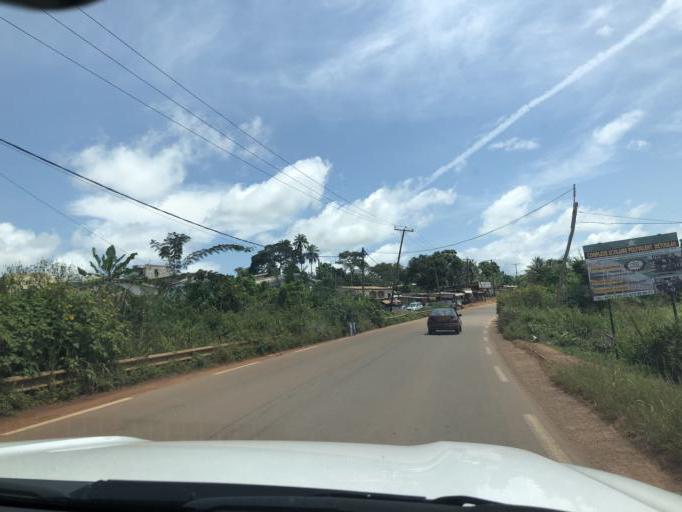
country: CM
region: Centre
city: Yaounde
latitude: 3.8634
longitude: 11.6184
